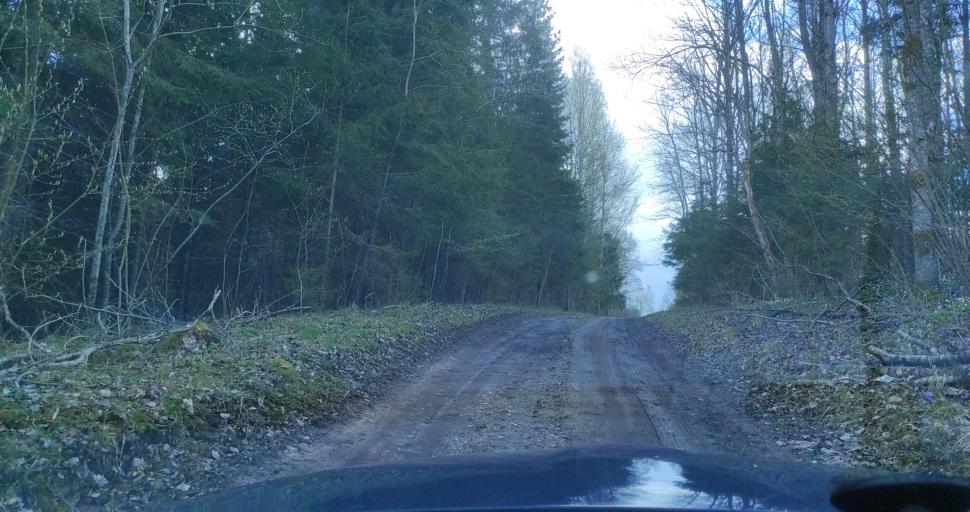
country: LV
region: Kuldigas Rajons
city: Kuldiga
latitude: 56.8630
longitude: 21.8304
